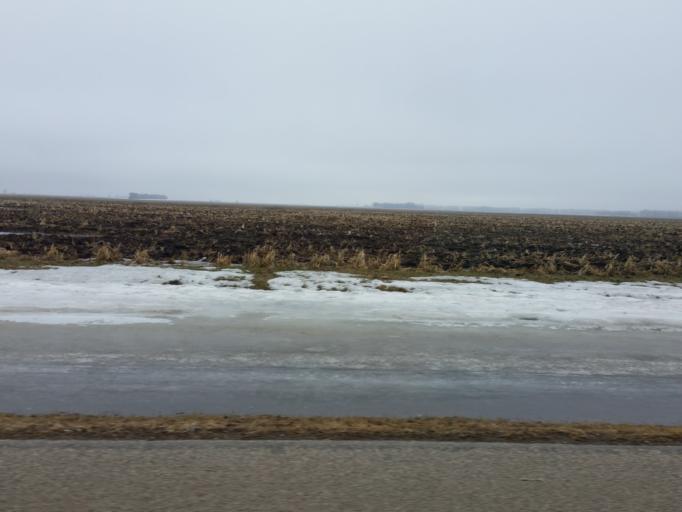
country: US
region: North Dakota
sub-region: Walsh County
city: Grafton
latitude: 48.6195
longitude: -97.4417
